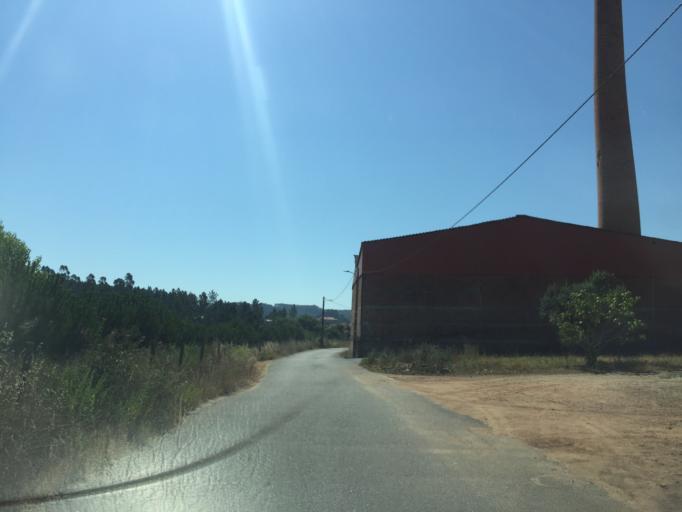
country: PT
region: Santarem
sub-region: Constancia
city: Constancia
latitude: 39.5380
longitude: -8.3178
